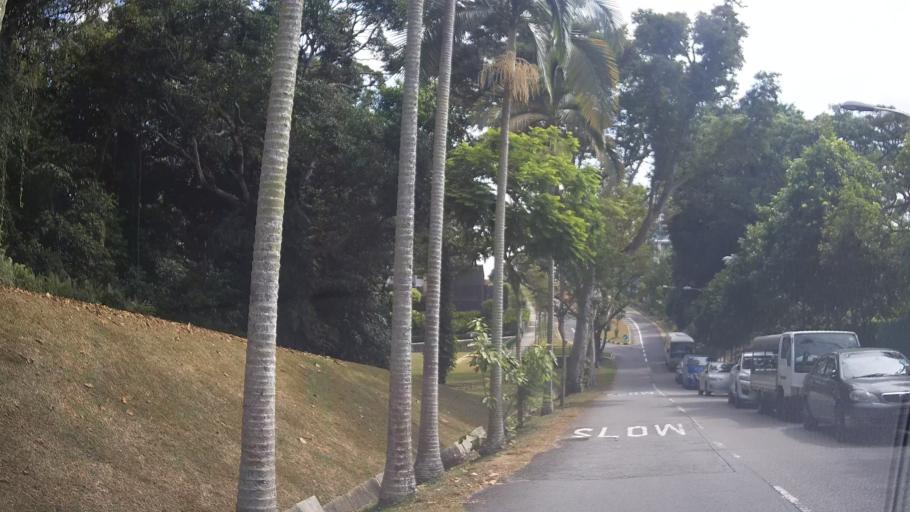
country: SG
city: Singapore
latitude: 1.3256
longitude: 103.9467
